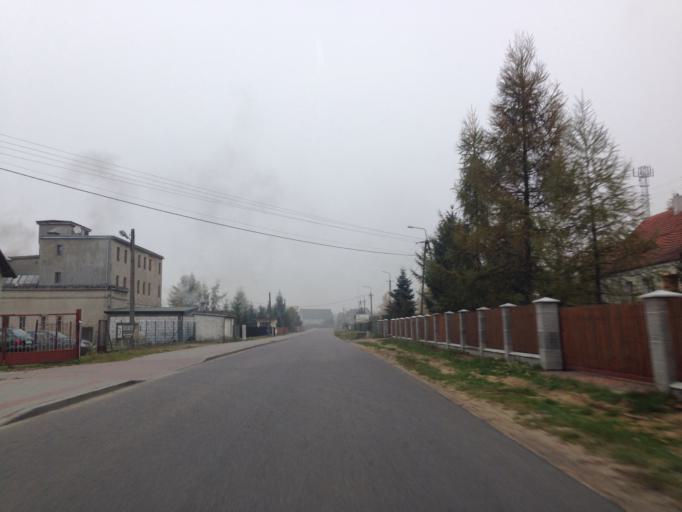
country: PL
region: Warmian-Masurian Voivodeship
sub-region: Powiat nowomiejski
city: Biskupiec
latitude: 53.4850
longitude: 19.3816
